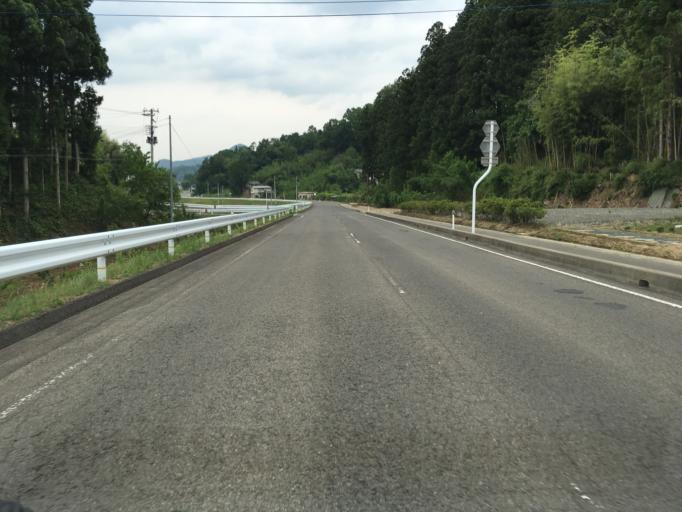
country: JP
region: Fukushima
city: Nihommatsu
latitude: 37.6423
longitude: 140.5356
